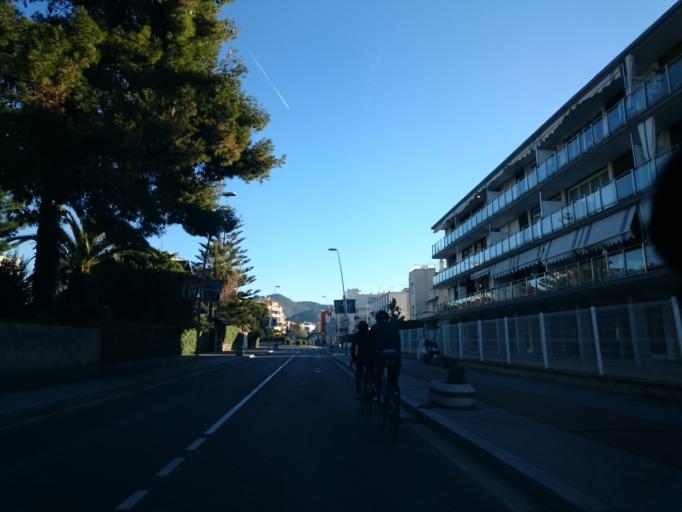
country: ES
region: Catalonia
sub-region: Provincia de Barcelona
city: Sitges
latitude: 41.2364
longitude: 1.8012
